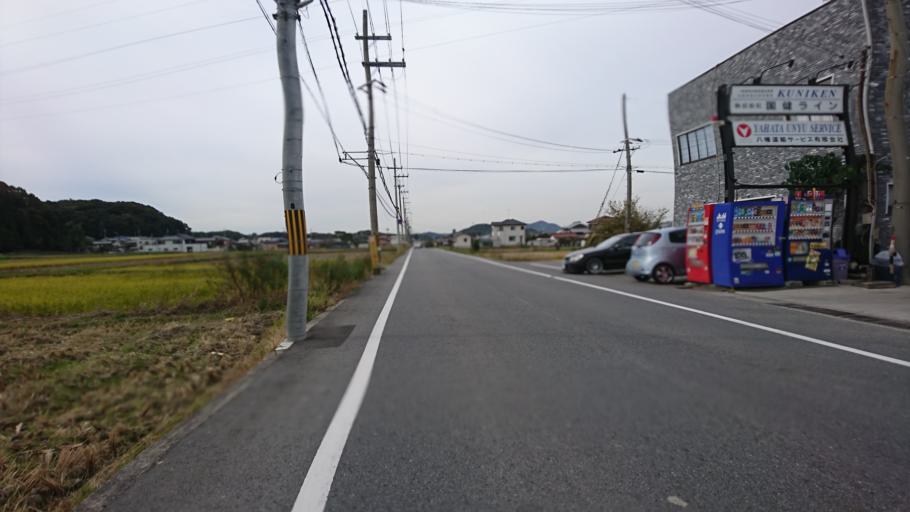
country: JP
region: Hyogo
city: Ono
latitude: 34.7842
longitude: 134.9143
